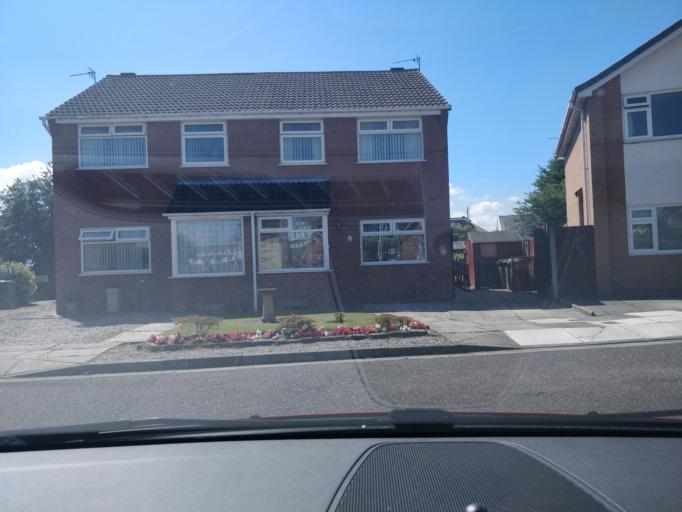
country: GB
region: England
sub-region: Lancashire
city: Banks
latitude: 53.6735
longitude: -2.9445
